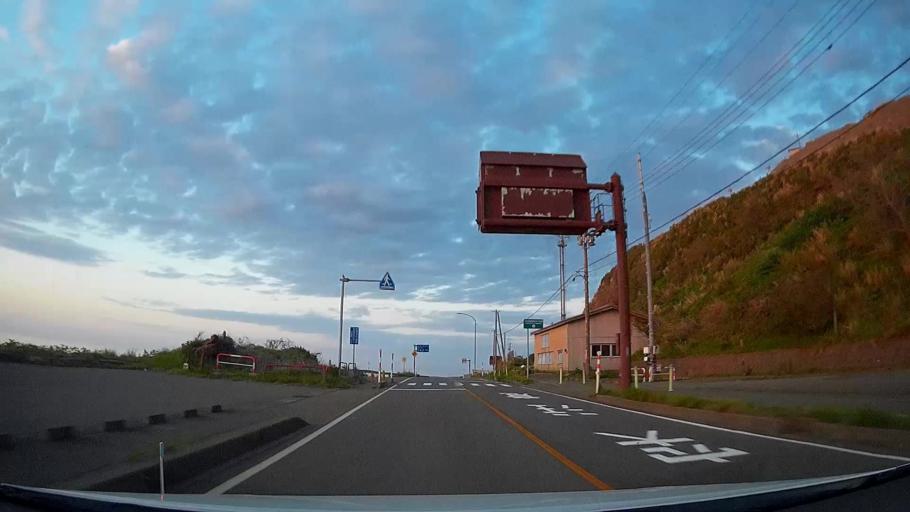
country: JP
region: Niigata
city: Joetsu
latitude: 37.1717
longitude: 138.0946
